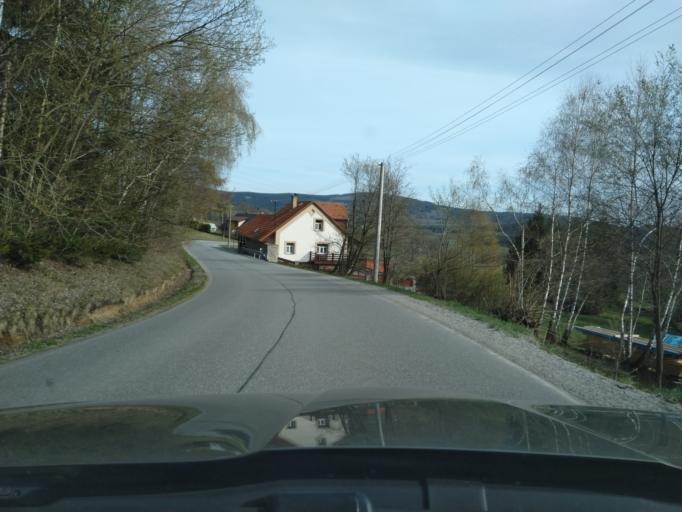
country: CZ
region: Jihocesky
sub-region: Okres Prachatice
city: Stachy
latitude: 49.0917
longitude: 13.6462
